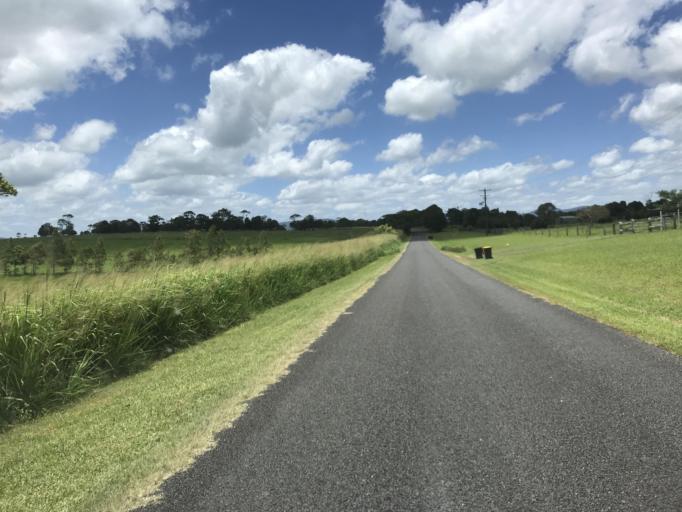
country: AU
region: Queensland
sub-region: Tablelands
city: Atherton
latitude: -17.3387
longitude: 145.5781
